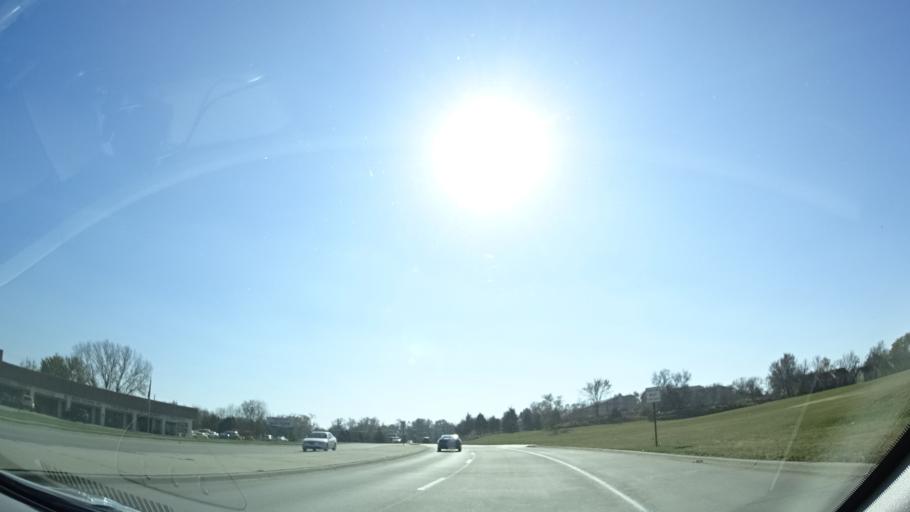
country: US
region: Nebraska
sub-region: Sarpy County
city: Offutt Air Force Base
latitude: 41.1380
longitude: -95.9677
